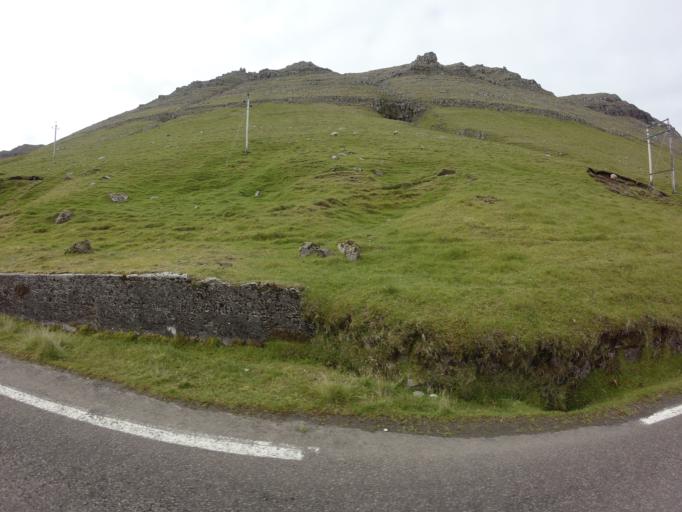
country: FO
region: Suduroy
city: Tvoroyri
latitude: 61.5765
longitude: -6.9382
